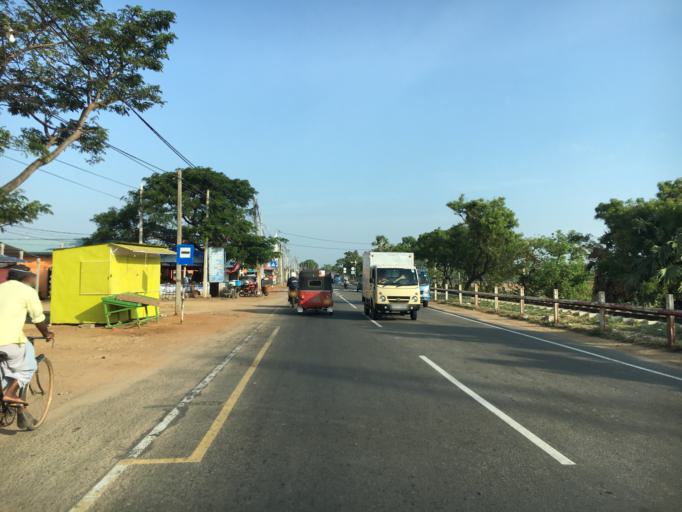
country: LK
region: Eastern Province
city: Eravur Town
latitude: 7.9173
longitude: 81.5194
